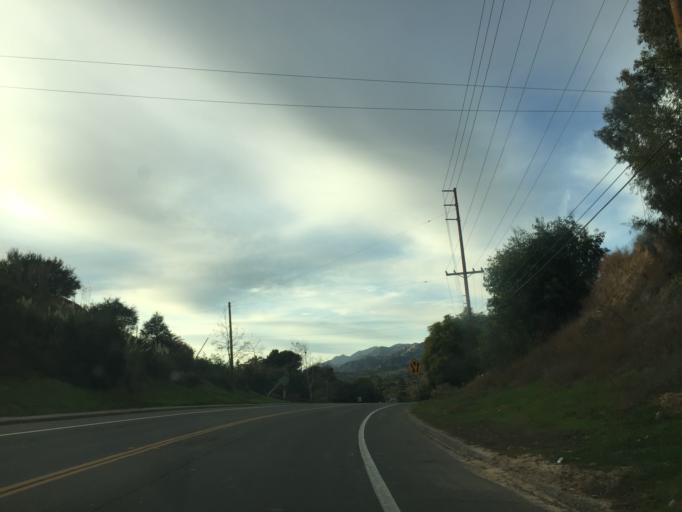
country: US
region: California
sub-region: Santa Barbara County
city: Goleta
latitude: 34.4518
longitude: -119.8044
